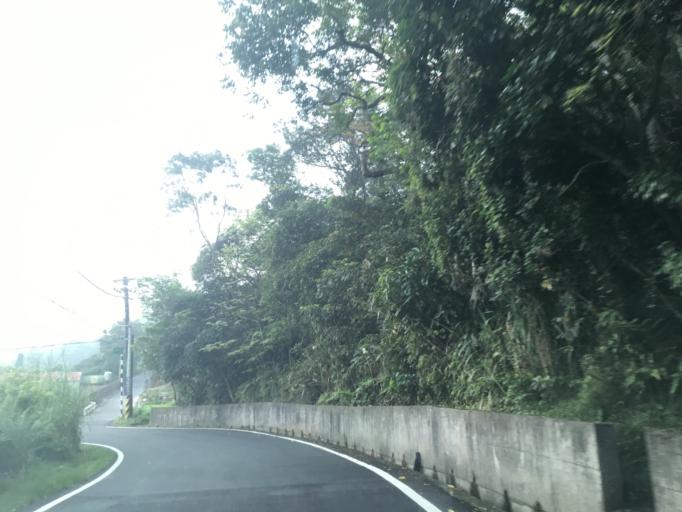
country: TW
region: Taiwan
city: Daxi
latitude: 24.8777
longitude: 121.3068
